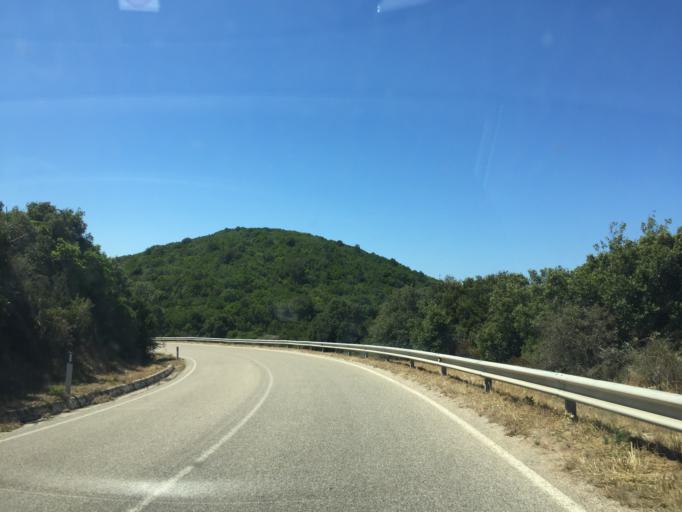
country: IT
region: Sardinia
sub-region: Provincia di Olbia-Tempio
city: Aglientu
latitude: 41.0895
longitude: 9.1053
